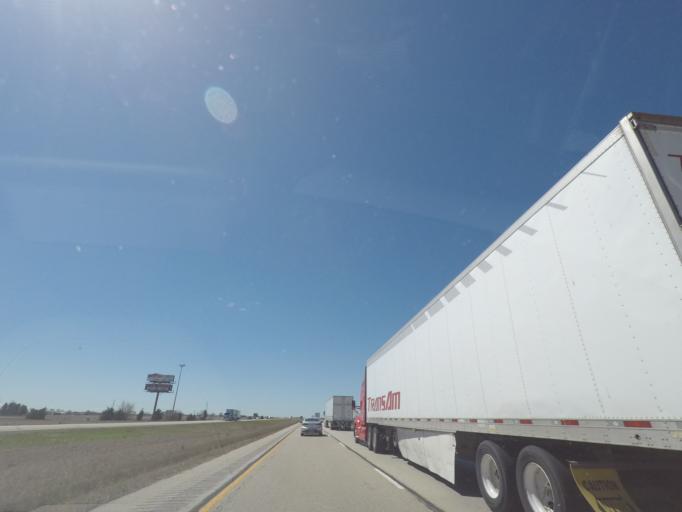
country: US
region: Illinois
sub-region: McLean County
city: Hudson
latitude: 40.5704
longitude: -88.9028
